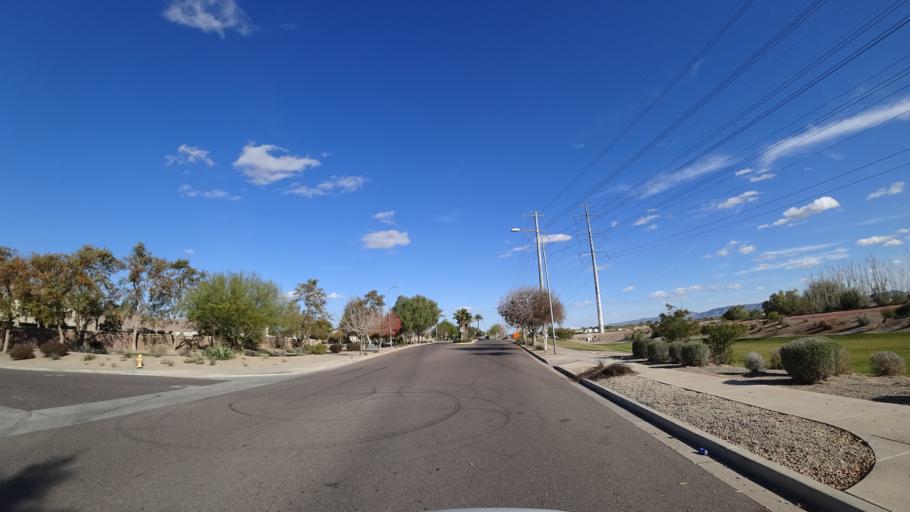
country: US
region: Arizona
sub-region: Maricopa County
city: Tolleson
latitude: 33.4160
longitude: -112.2398
